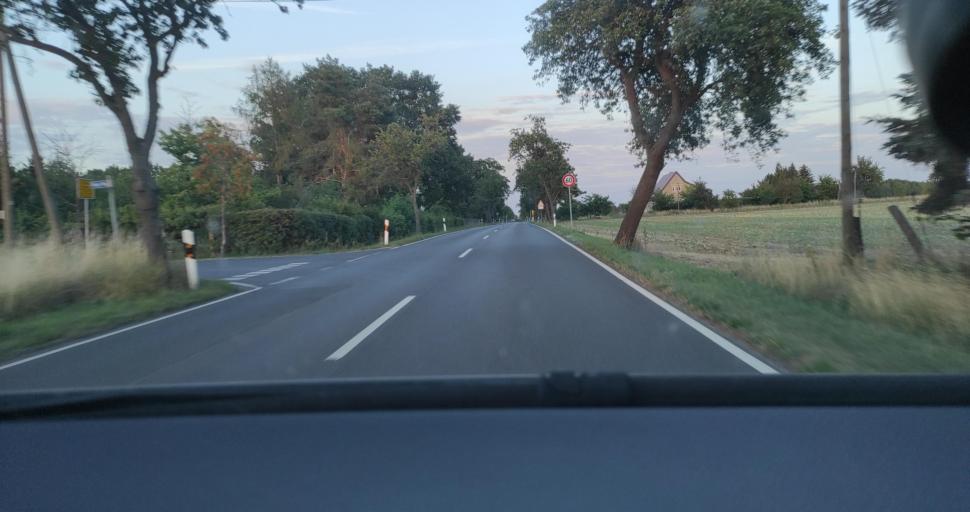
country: DE
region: Brandenburg
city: Heinersbruck
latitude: 51.7260
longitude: 14.5337
